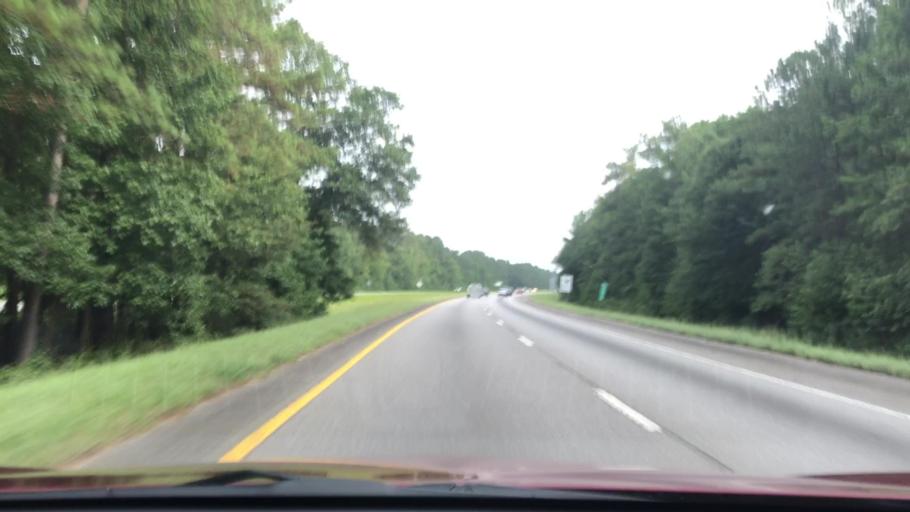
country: US
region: South Carolina
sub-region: Orangeburg County
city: Holly Hill
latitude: 33.2911
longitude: -80.5209
